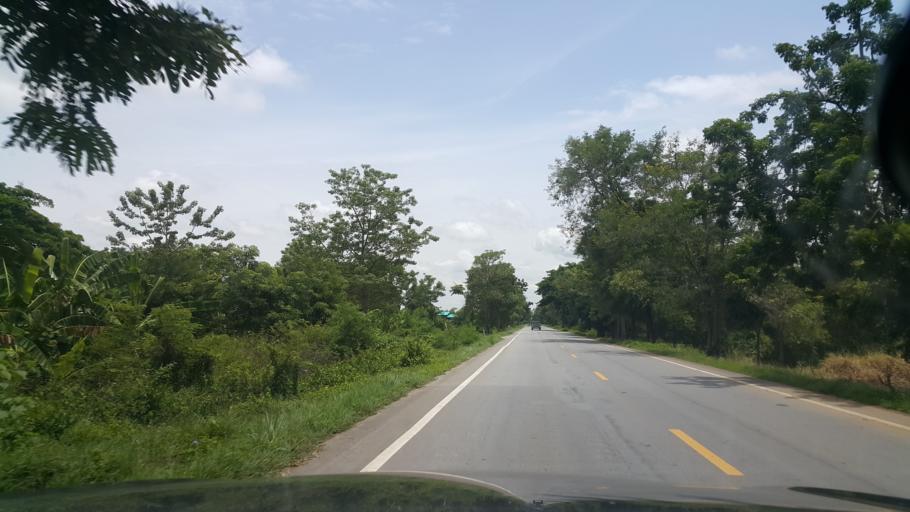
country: TH
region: Sukhothai
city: Sawankhalok
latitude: 17.3564
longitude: 99.7422
